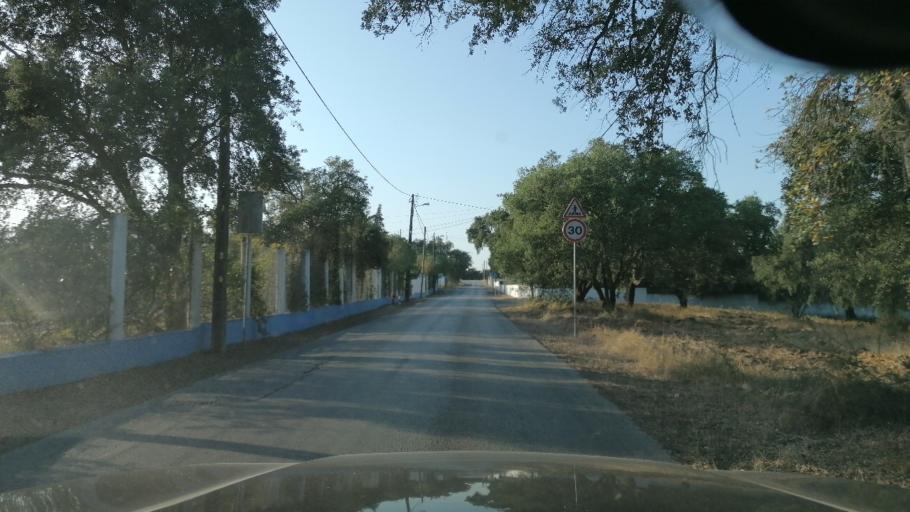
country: PT
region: Setubal
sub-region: Setubal
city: Setubal
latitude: 38.5463
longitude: -8.8406
